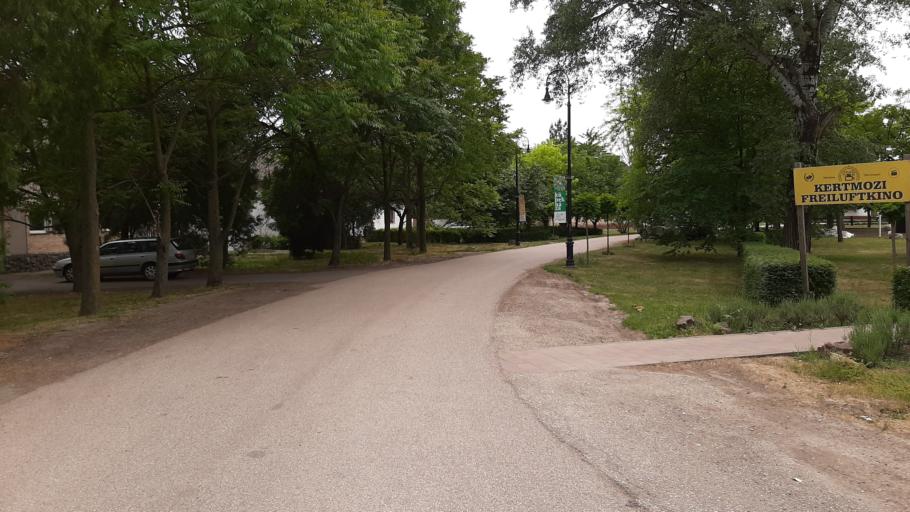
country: RO
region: Timis
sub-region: Comuna Beba Veche
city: Beba Veche
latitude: 46.1493
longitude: 20.2772
